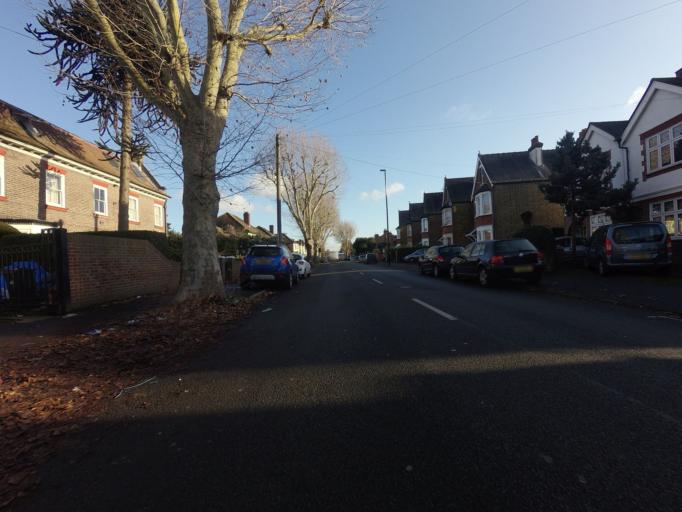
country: GB
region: England
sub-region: Greater London
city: Feltham
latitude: 51.4463
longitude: -0.4026
